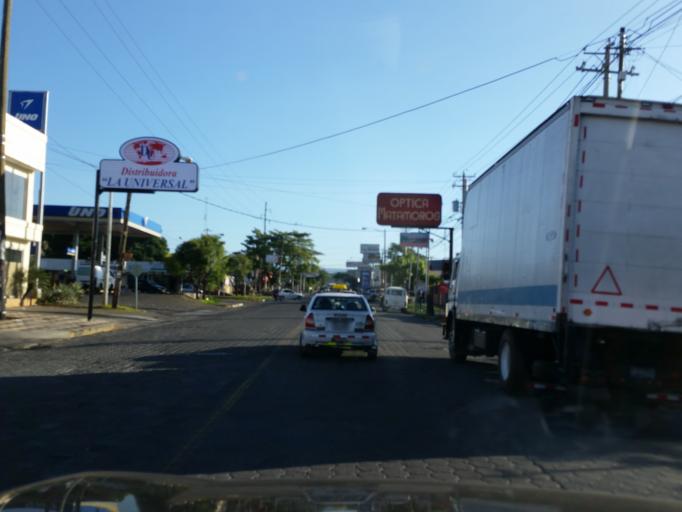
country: NI
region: Managua
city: Ciudad Sandino
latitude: 12.1514
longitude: -86.3046
